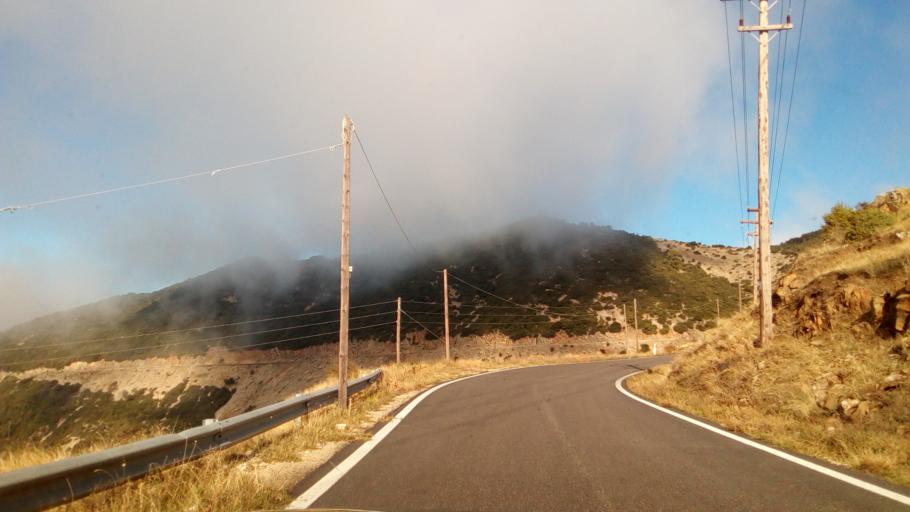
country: GR
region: West Greece
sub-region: Nomos Aitolias kai Akarnanias
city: Thermo
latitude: 38.5845
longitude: 21.7734
